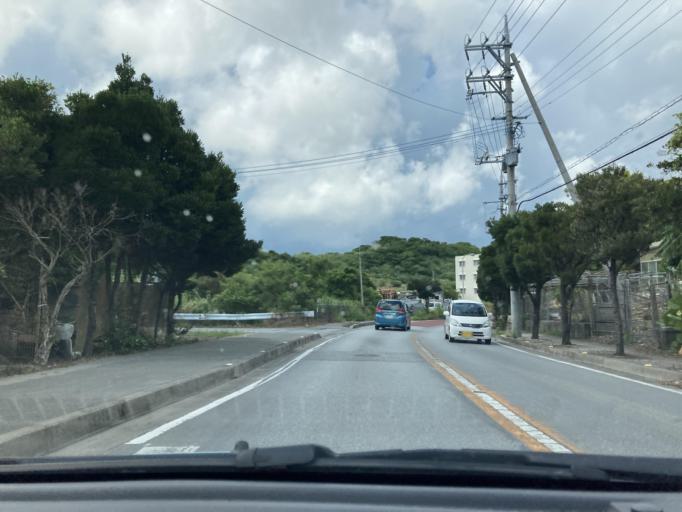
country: JP
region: Okinawa
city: Tomigusuku
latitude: 26.1708
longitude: 127.7534
